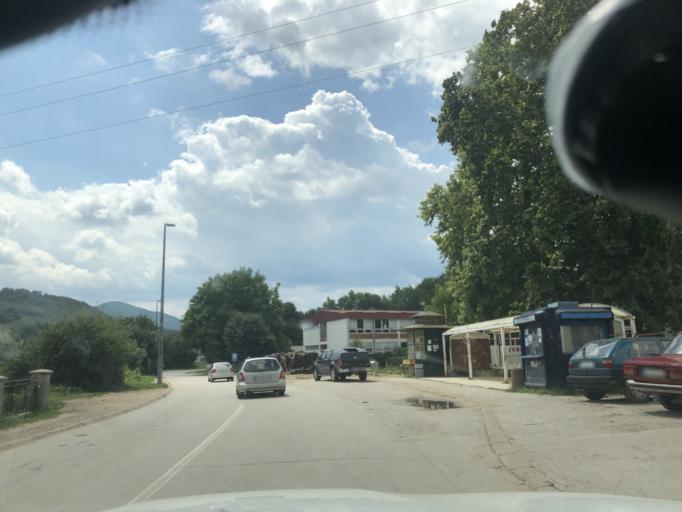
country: RS
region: Central Serbia
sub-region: Jablanicki Okrug
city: Medvega
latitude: 42.8429
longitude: 21.5872
